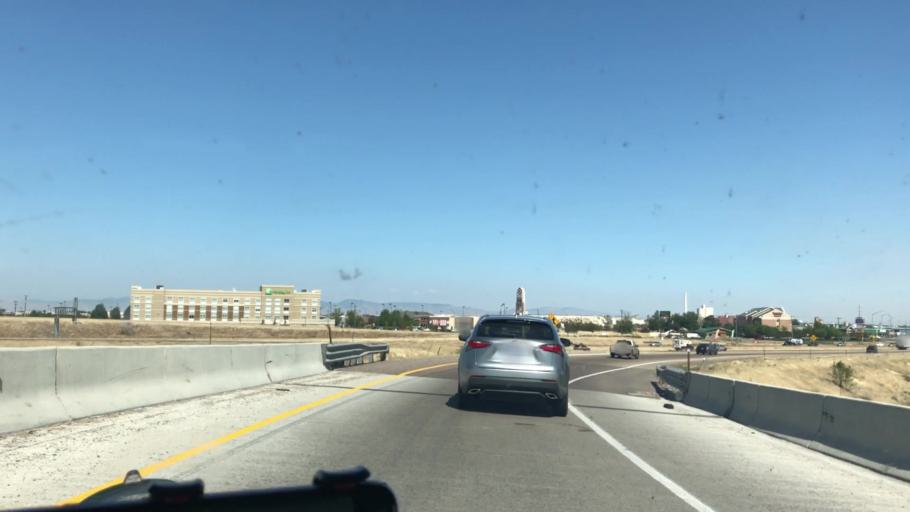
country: US
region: Idaho
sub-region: Canyon County
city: Nampa
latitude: 43.6085
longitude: -116.5976
